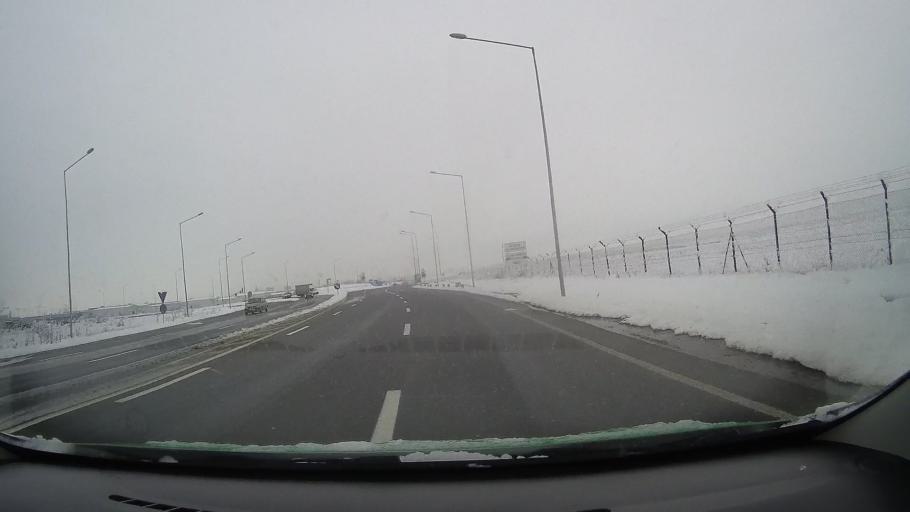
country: RO
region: Sibiu
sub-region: Comuna Cristian
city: Cristian
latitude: 45.7884
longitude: 24.0759
